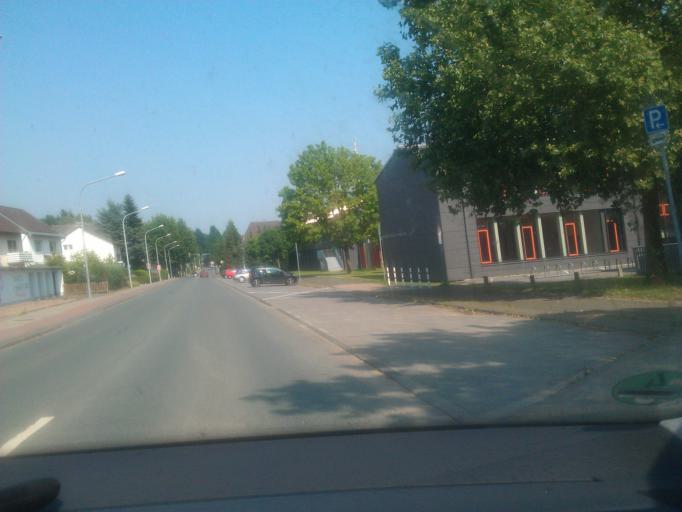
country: DE
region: North Rhine-Westphalia
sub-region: Regierungsbezirk Detmold
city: Lemgo
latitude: 52.0328
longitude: 8.8949
